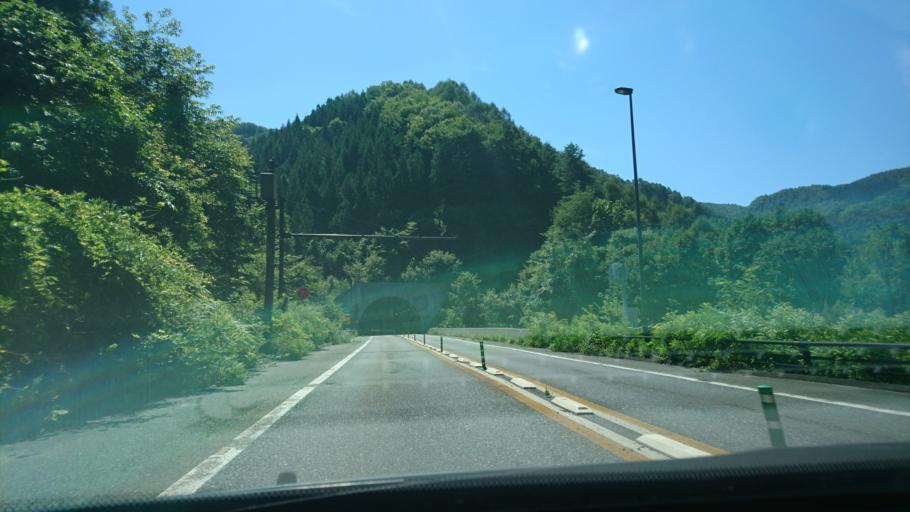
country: JP
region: Iwate
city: Tono
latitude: 39.2461
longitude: 141.6360
